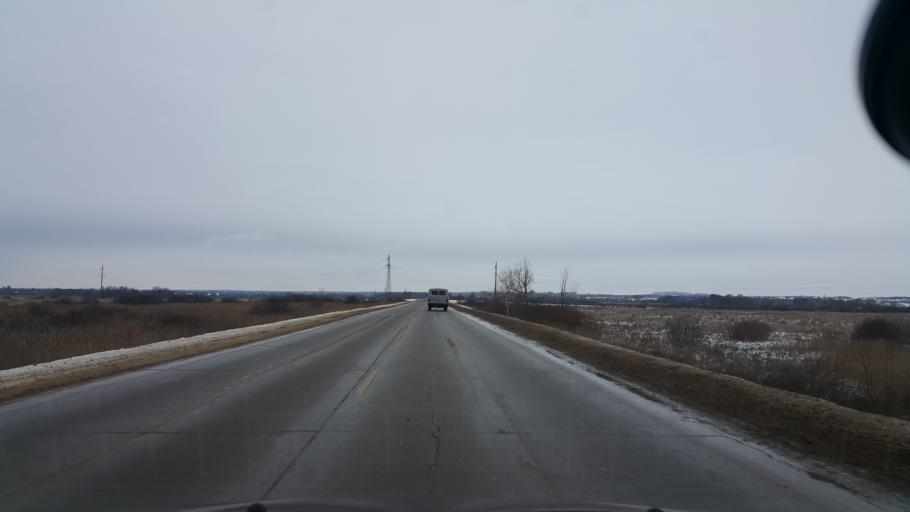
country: RU
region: Tambov
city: Bokino
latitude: 52.6239
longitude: 41.4859
